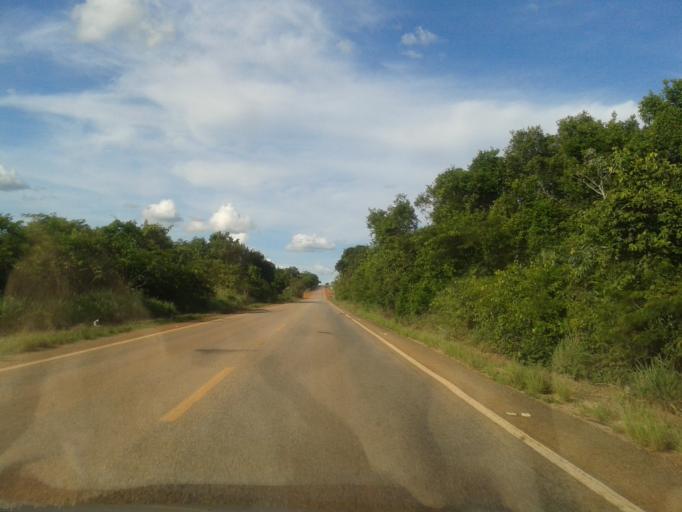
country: BR
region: Goias
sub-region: Mozarlandia
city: Mozarlandia
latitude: -14.4028
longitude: -50.4435
